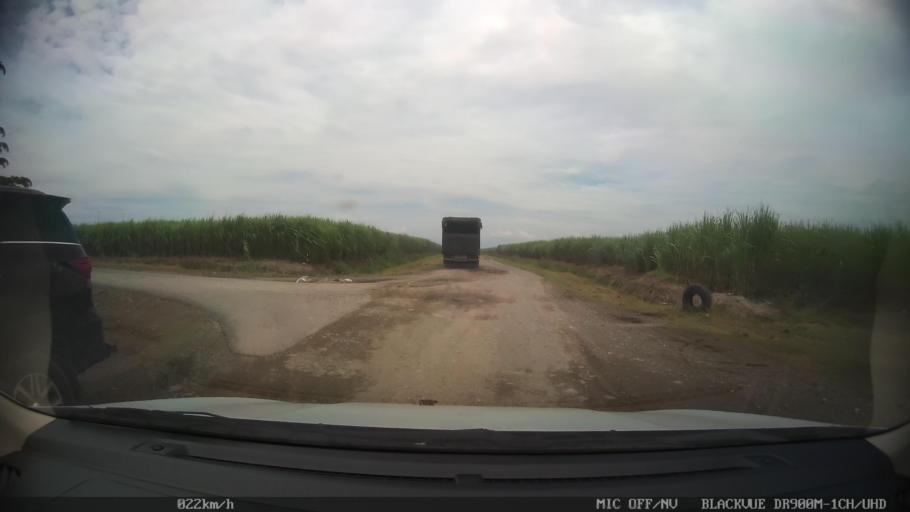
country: ID
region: North Sumatra
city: Sunggal
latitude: 3.6354
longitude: 98.5763
